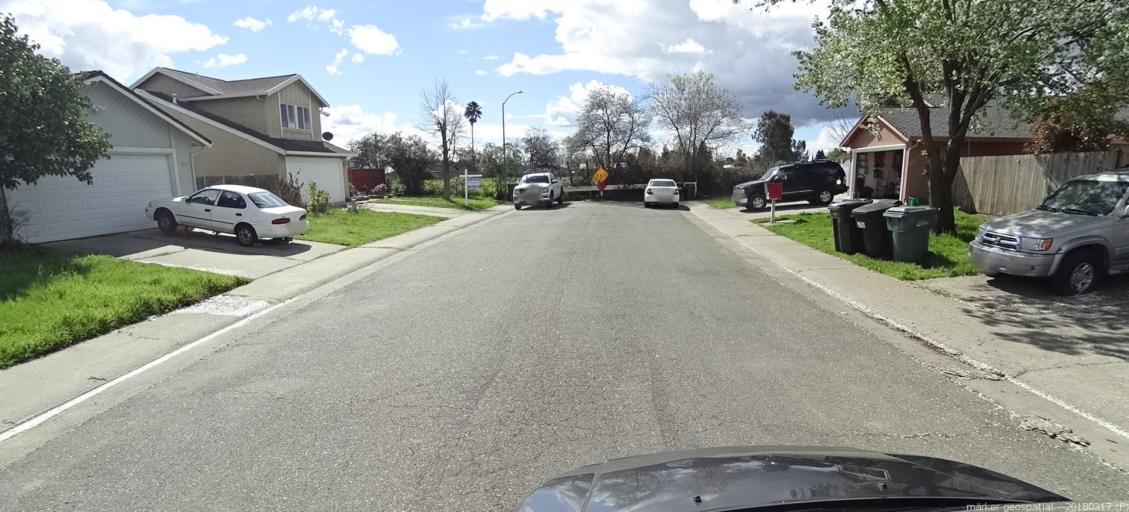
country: US
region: California
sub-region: Sacramento County
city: Florin
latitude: 38.4772
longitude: -121.4114
